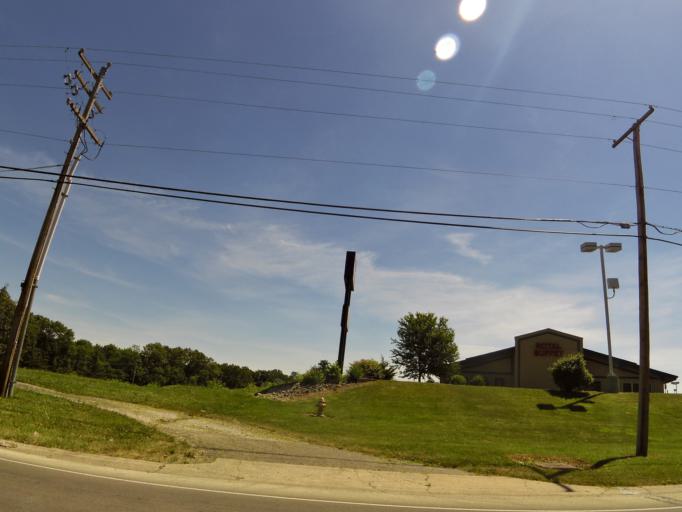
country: US
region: Illinois
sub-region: Vermilion County
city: Danville
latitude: 40.2031
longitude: -87.6310
